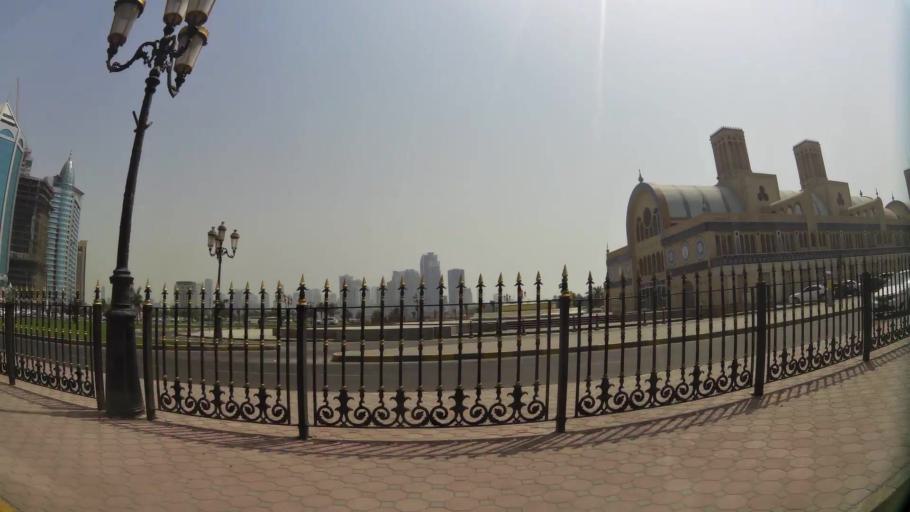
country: AE
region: Ash Shariqah
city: Sharjah
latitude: 25.3469
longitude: 55.3844
